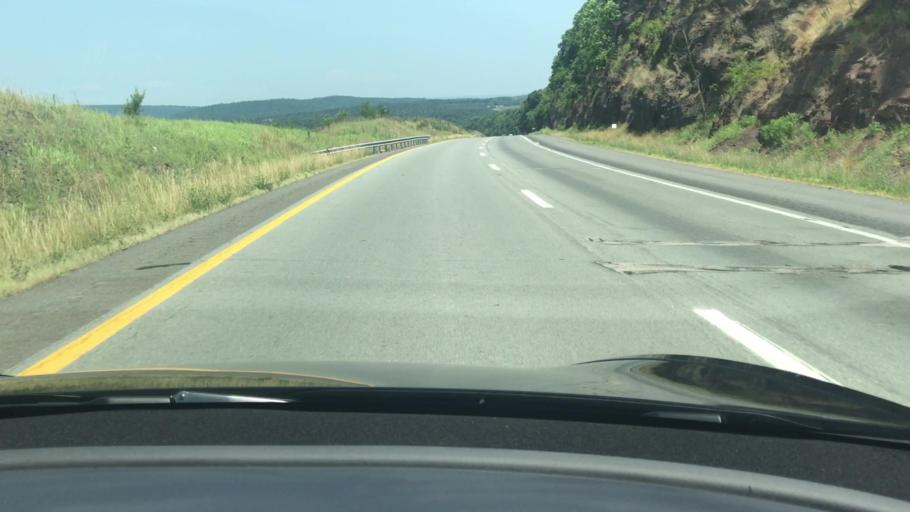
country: US
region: Pennsylvania
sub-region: Perry County
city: Newport
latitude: 40.5025
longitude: -77.1285
